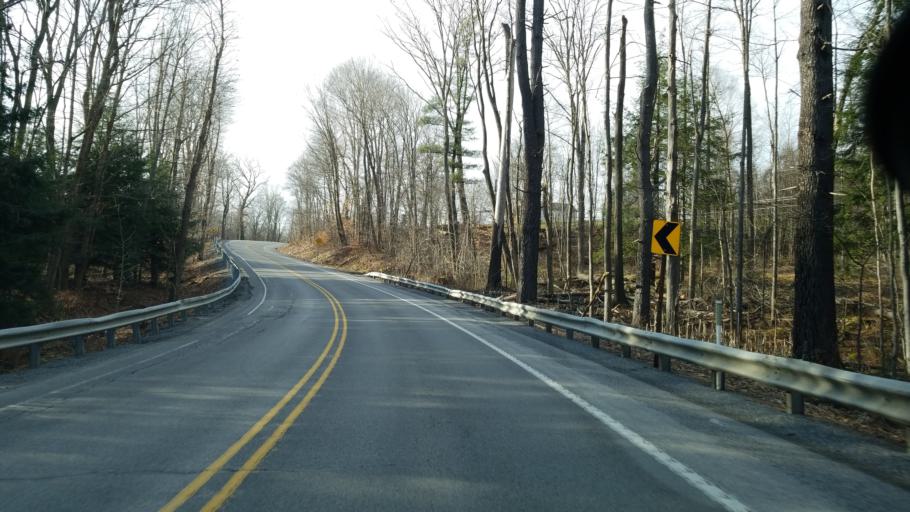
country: US
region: Pennsylvania
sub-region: Clearfield County
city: Curwensville
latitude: 40.9724
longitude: -78.6200
